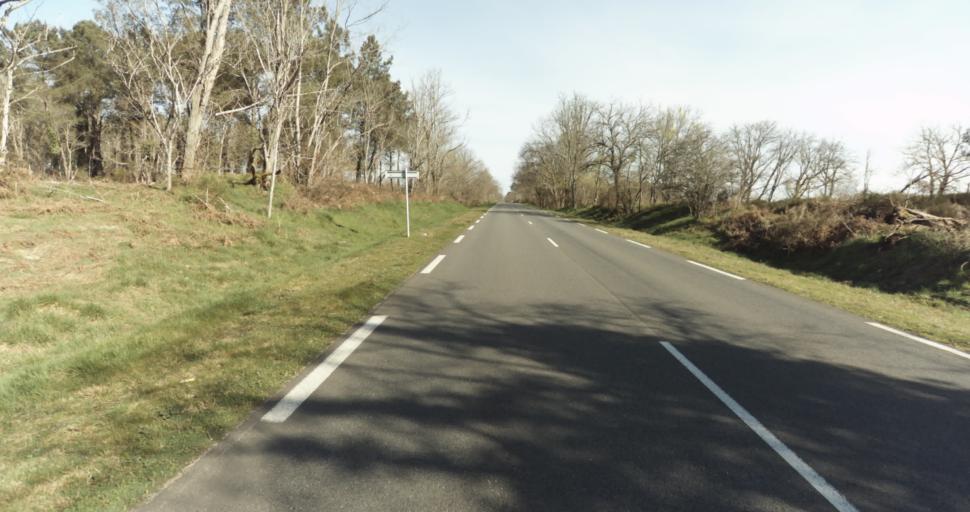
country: FR
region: Aquitaine
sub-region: Departement des Landes
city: Roquefort
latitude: 44.0676
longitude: -0.3155
